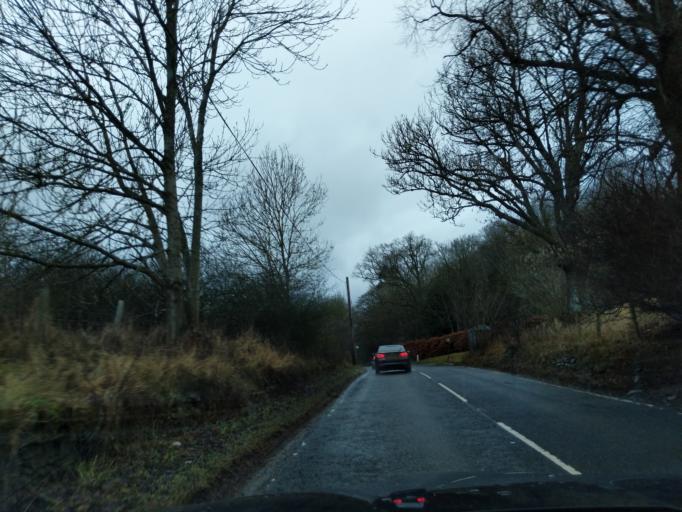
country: GB
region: Scotland
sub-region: The Scottish Borders
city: Galashiels
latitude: 55.6439
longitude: -2.8499
